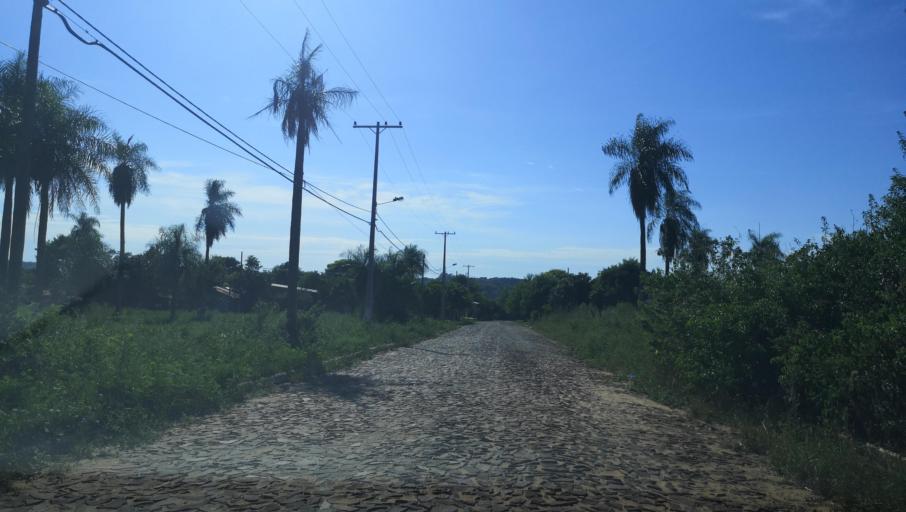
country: PY
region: Misiones
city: Santa Maria
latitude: -26.8770
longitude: -57.0083
